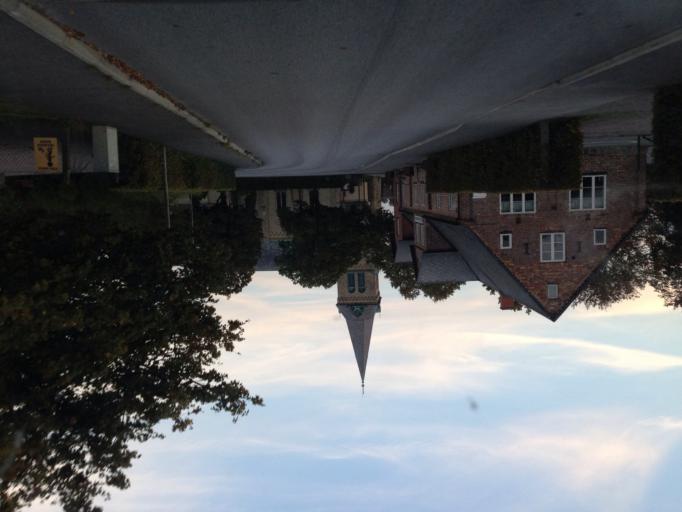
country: SE
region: Skane
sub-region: Lomma Kommun
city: Lomma
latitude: 55.6872
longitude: 13.0792
